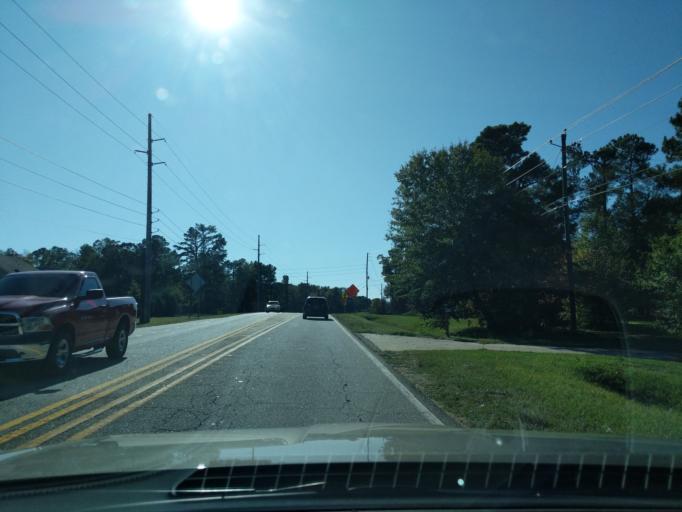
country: US
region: Georgia
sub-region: Columbia County
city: Grovetown
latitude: 33.4620
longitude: -82.1792
